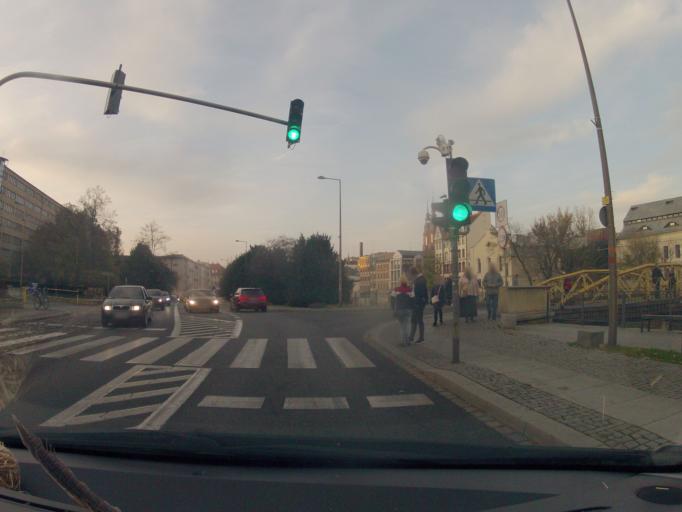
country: PL
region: Opole Voivodeship
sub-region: Powiat opolski
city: Opole
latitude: 50.6673
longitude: 17.9207
